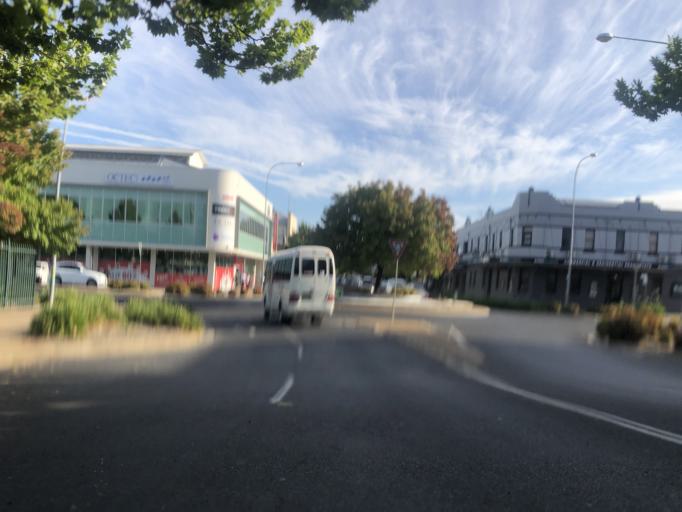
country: AU
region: New South Wales
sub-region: Orange Municipality
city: Orange
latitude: -33.2862
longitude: 149.1007
